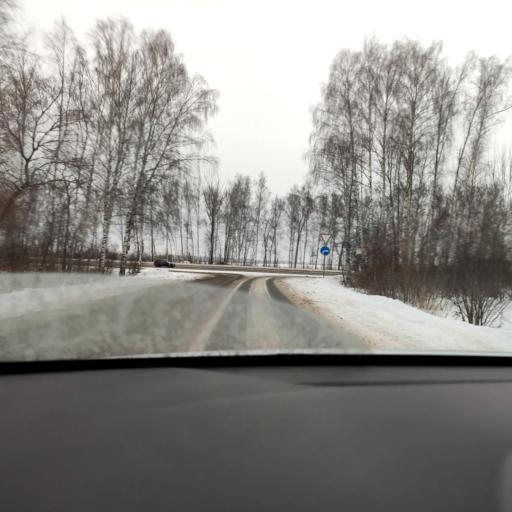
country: RU
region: Tatarstan
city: Osinovo
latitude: 55.8608
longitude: 48.8204
